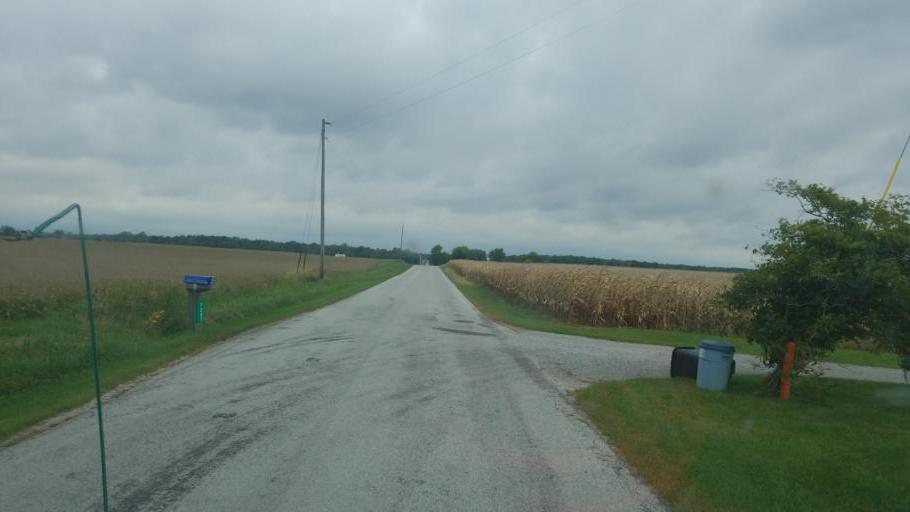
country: US
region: Ohio
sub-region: Seneca County
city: Fostoria
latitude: 41.0610
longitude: -83.4962
